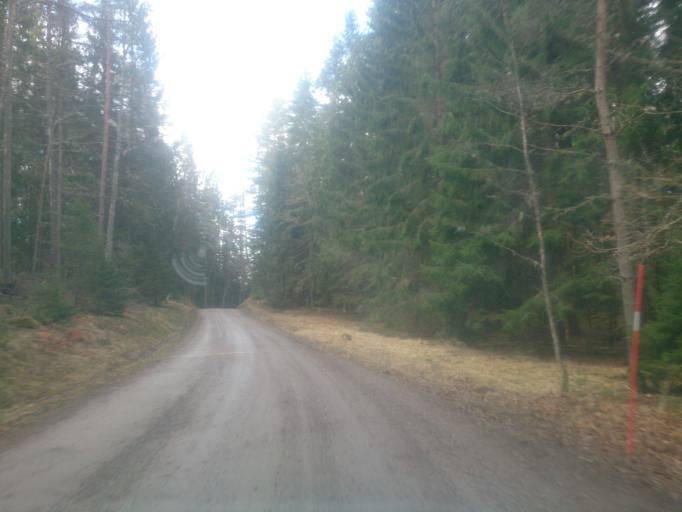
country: SE
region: OEstergoetland
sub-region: Atvidabergs Kommun
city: Atvidaberg
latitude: 58.2132
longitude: 16.1708
